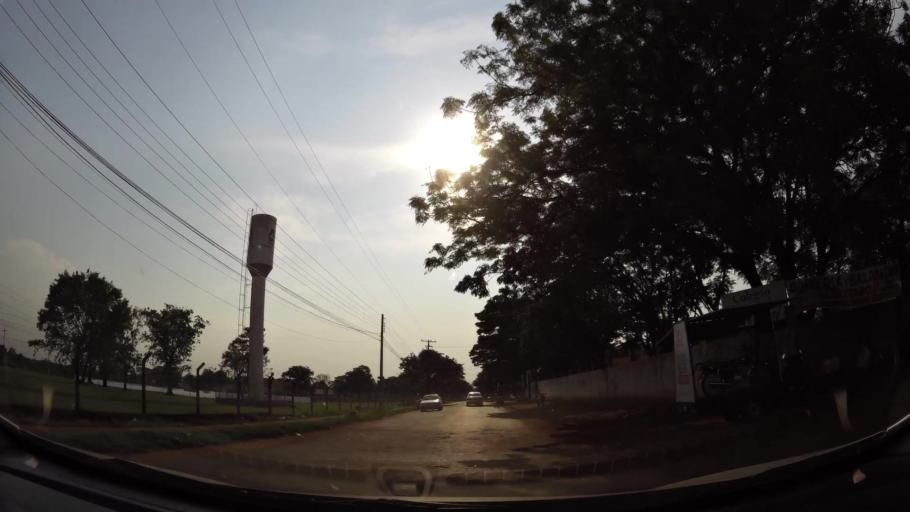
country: PY
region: Alto Parana
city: Ciudad del Este
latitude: -25.4834
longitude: -54.6665
